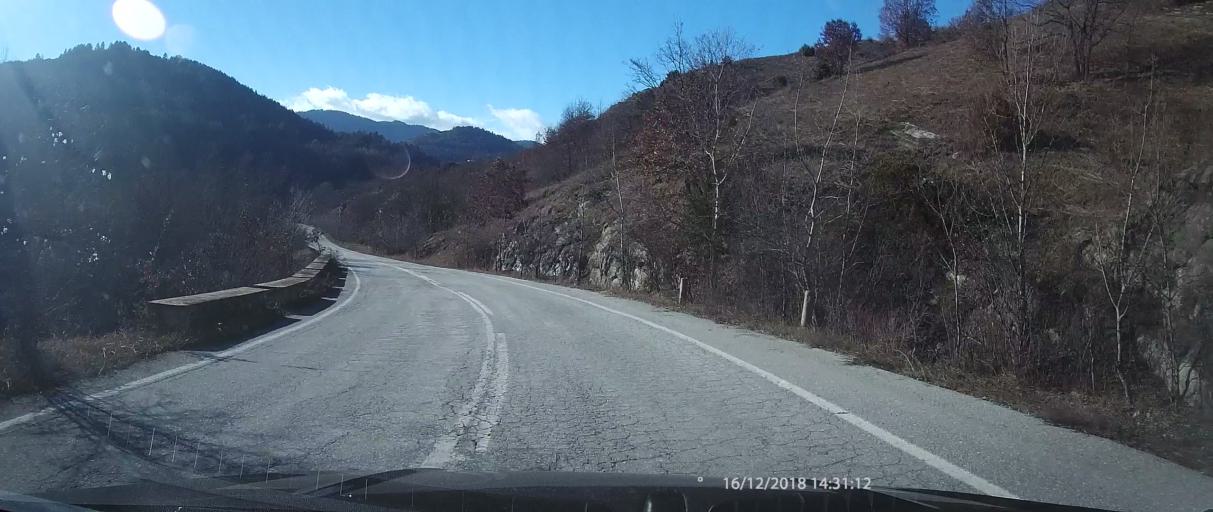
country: GR
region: West Macedonia
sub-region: Nomos Kozanis
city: Tsotili
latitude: 40.1942
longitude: 21.1842
